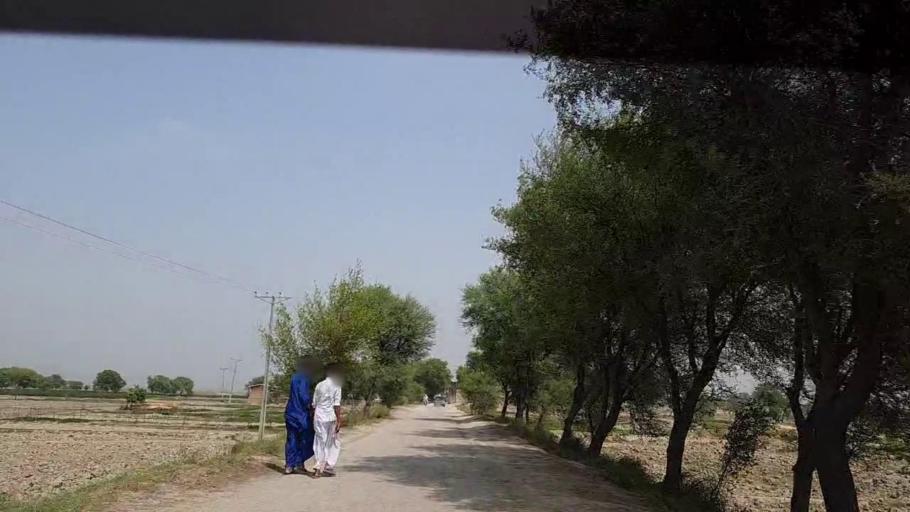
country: PK
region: Sindh
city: Khairpur Nathan Shah
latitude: 27.0783
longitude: 67.6853
